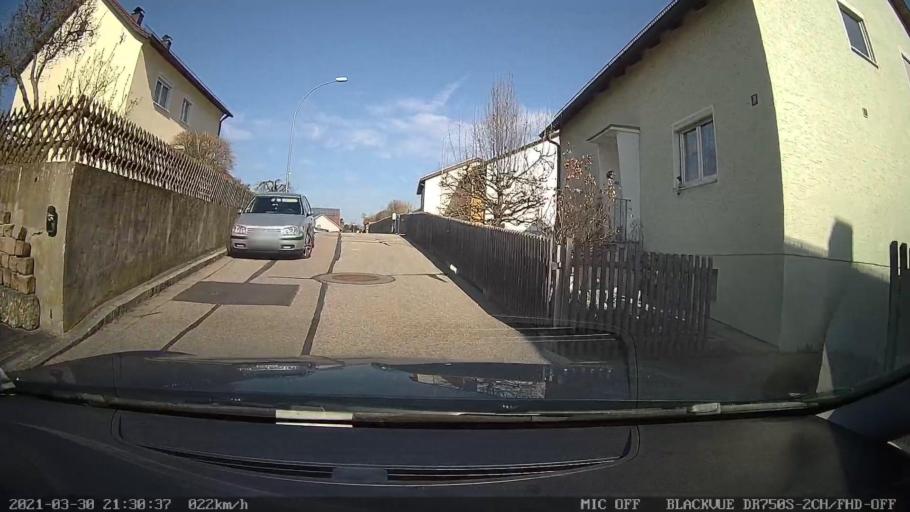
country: DE
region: Bavaria
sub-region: Upper Palatinate
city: Zeitlarn
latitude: 49.0963
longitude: 12.1054
